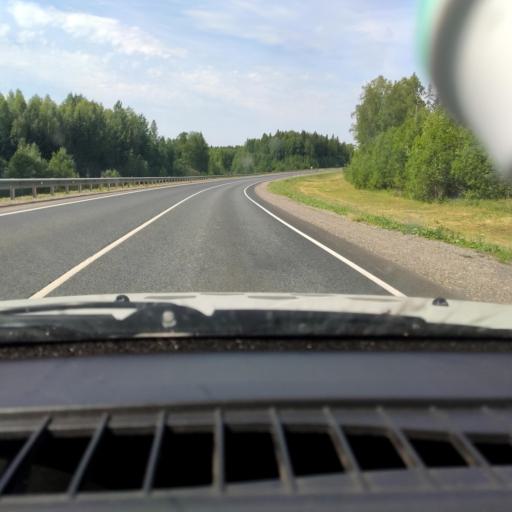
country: RU
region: Kirov
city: Kostino
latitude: 58.7502
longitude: 53.6112
